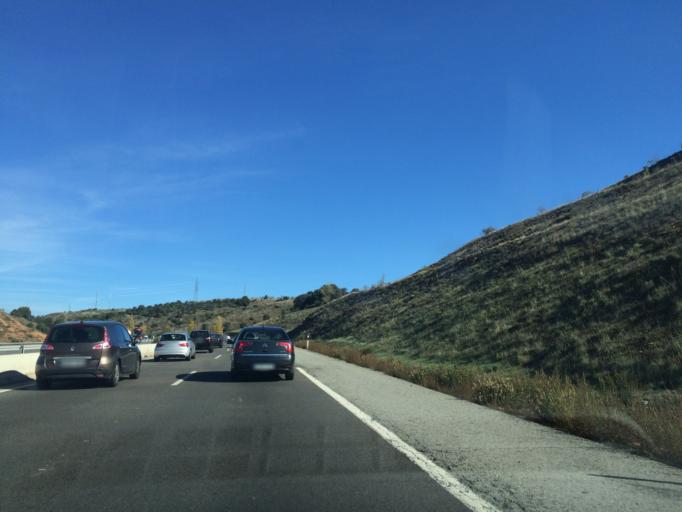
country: ES
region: Madrid
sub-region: Provincia de Madrid
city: Cabanillas de la Sierra
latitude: 40.8106
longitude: -3.6183
